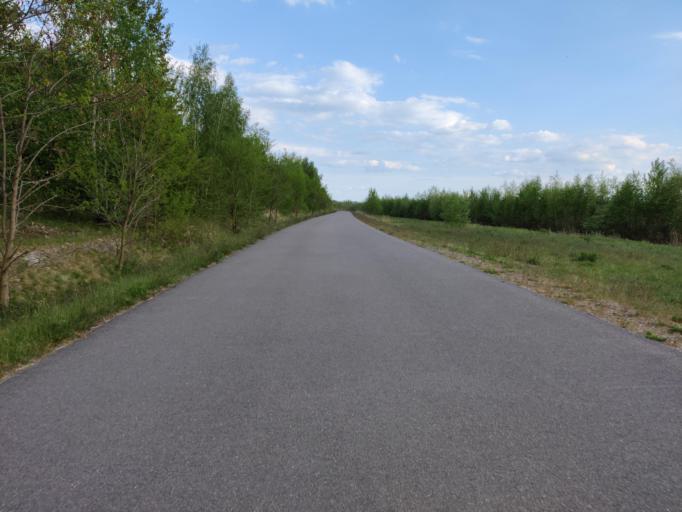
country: DE
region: Saxony
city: Rotha
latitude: 51.2221
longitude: 12.4416
